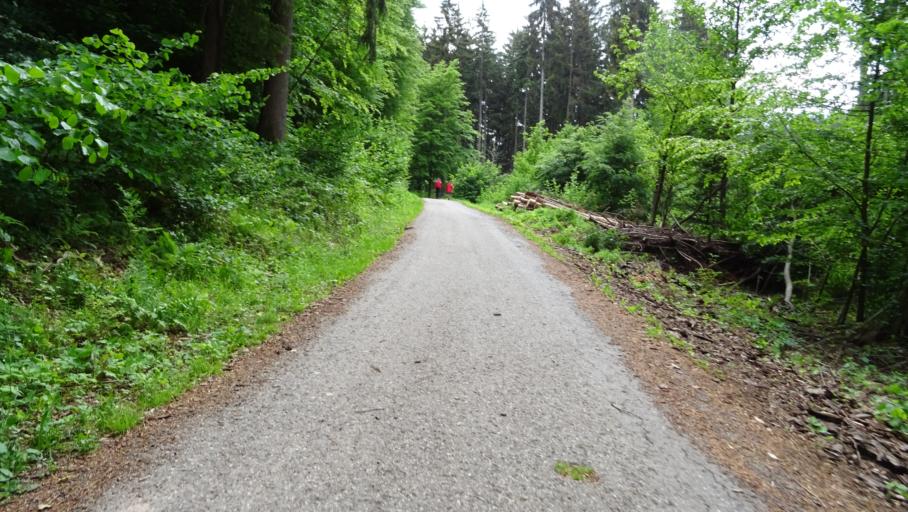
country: DE
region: Baden-Wuerttemberg
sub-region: Karlsruhe Region
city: Fahrenbach
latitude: 49.3938
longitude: 9.1755
